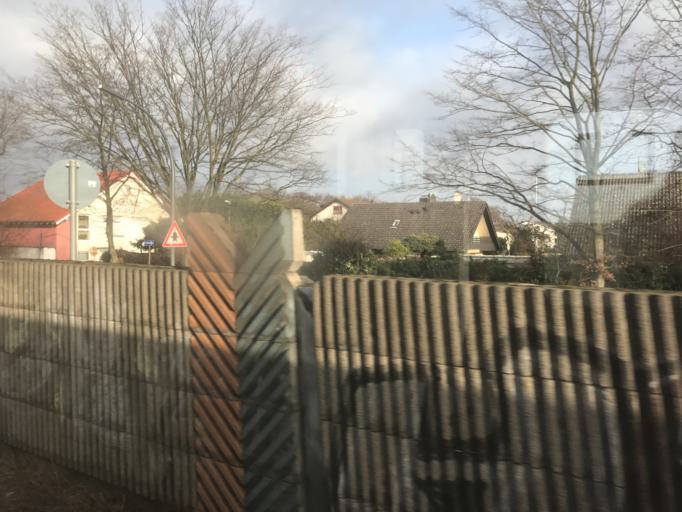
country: DE
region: North Rhine-Westphalia
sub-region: Regierungsbezirk Koln
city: Muelheim
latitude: 50.9813
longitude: 7.0089
